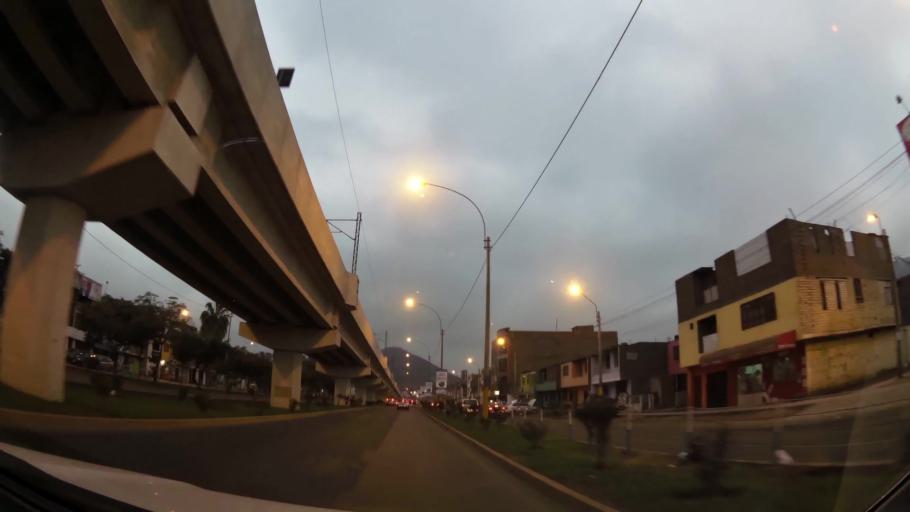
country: PE
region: Lima
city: Lima
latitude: -12.0223
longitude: -77.0069
